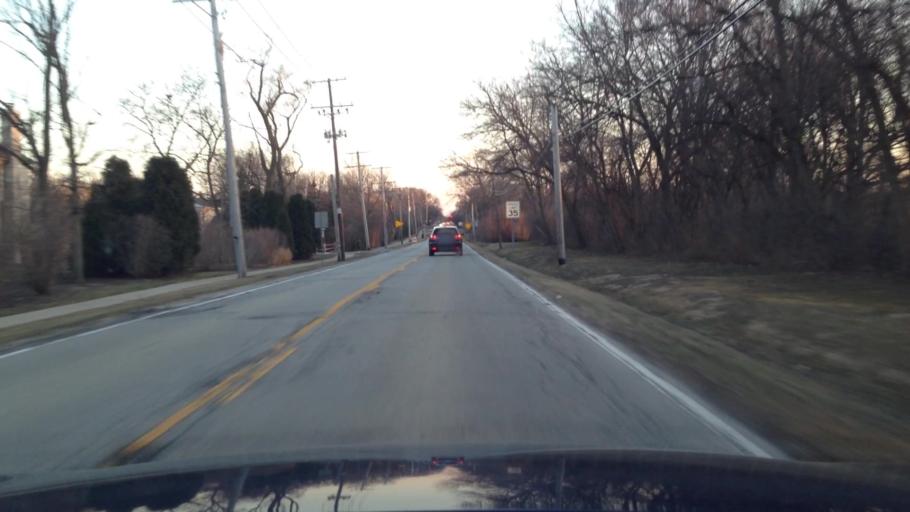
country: US
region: Illinois
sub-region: Cook County
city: Northfield
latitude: 42.1141
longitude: -87.7901
